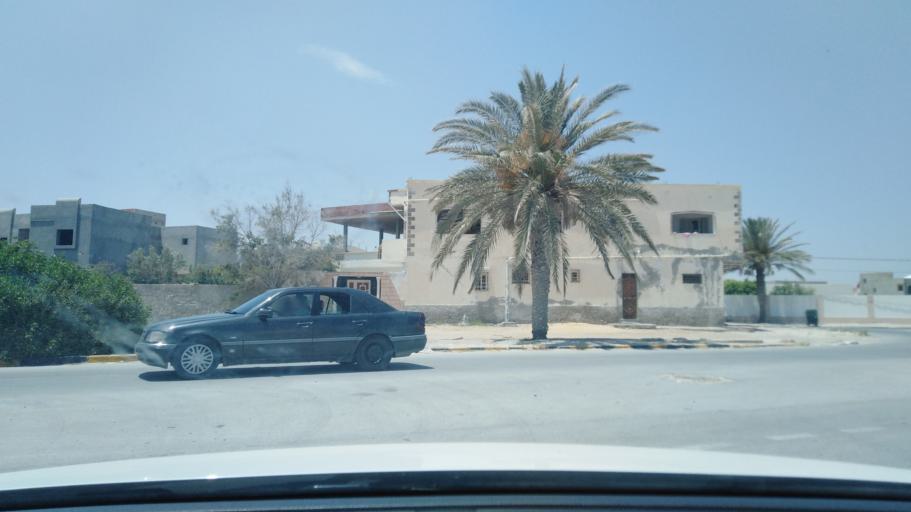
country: TN
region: Qabis
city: Gabes
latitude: 33.9487
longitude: 10.0699
